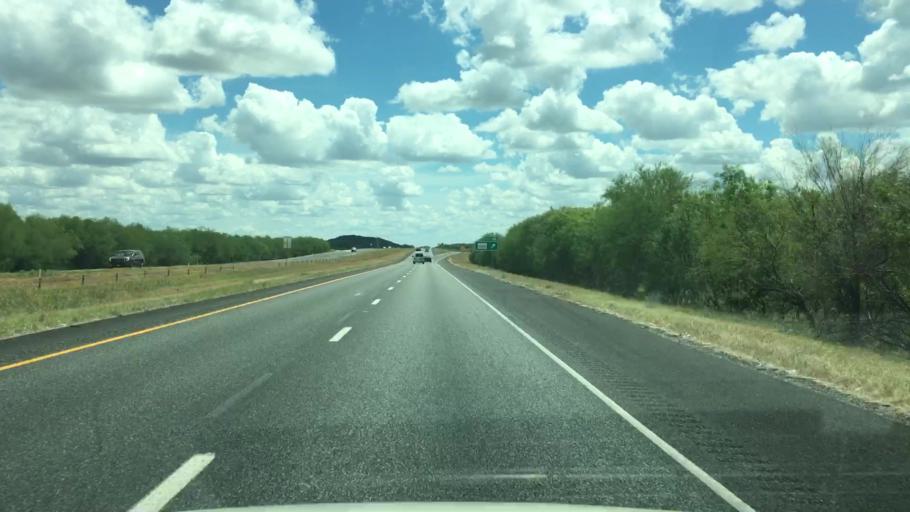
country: US
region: Texas
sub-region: Atascosa County
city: Pleasanton
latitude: 28.7404
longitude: -98.2917
